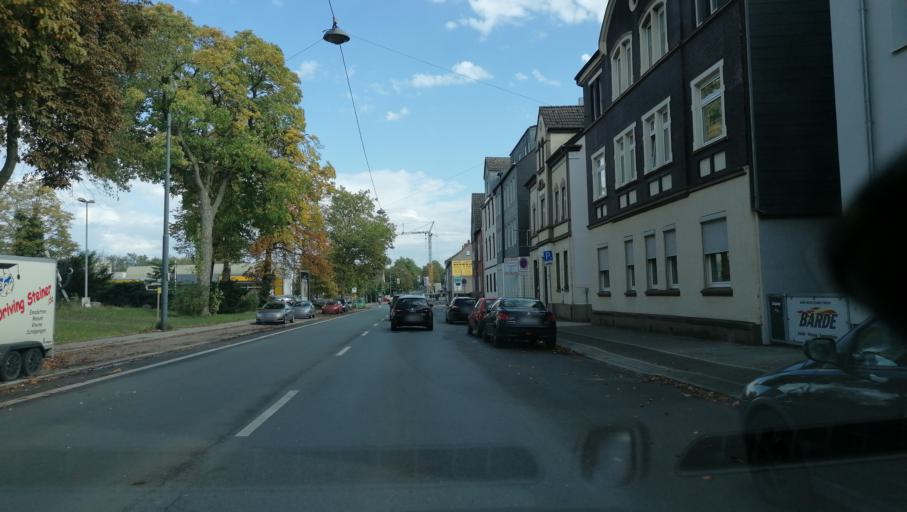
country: DE
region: North Rhine-Westphalia
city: Herten
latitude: 51.6024
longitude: 7.1583
